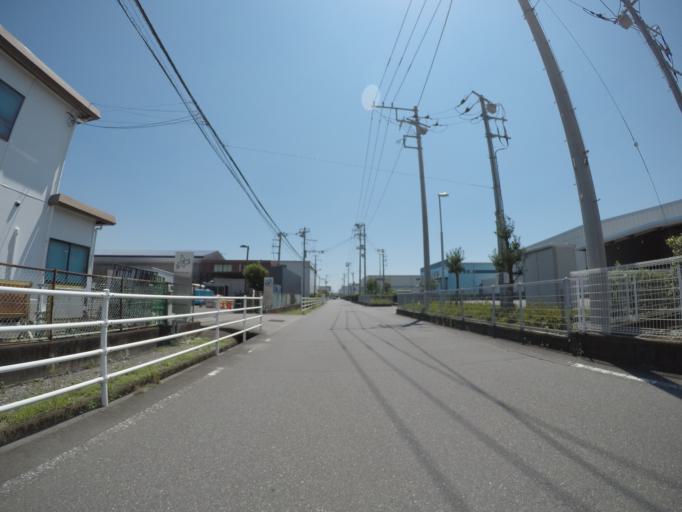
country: JP
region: Shizuoka
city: Fuji
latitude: 35.1353
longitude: 138.6411
